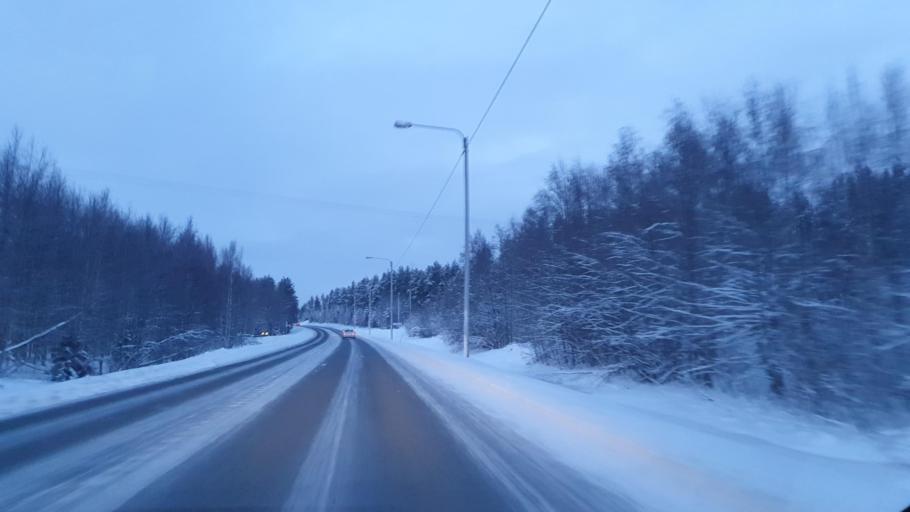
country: FI
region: Northern Ostrobothnia
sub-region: Oulu
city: Tyrnaevae
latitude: 64.9235
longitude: 25.7519
